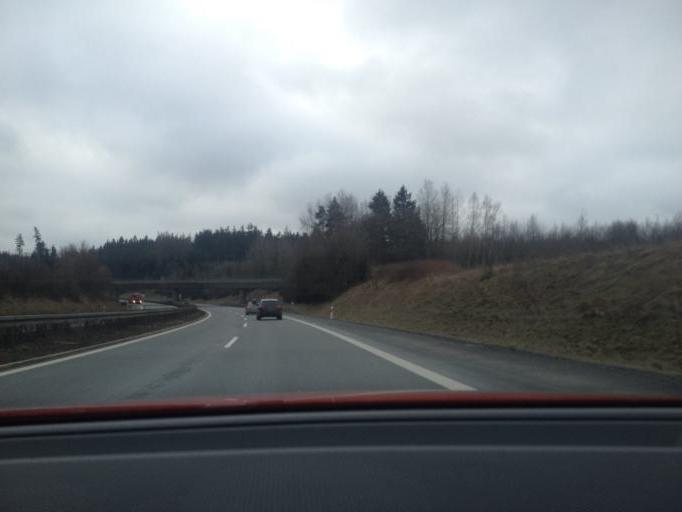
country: DE
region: Bavaria
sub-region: Upper Franconia
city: Schonwald
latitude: 50.1959
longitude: 12.1005
